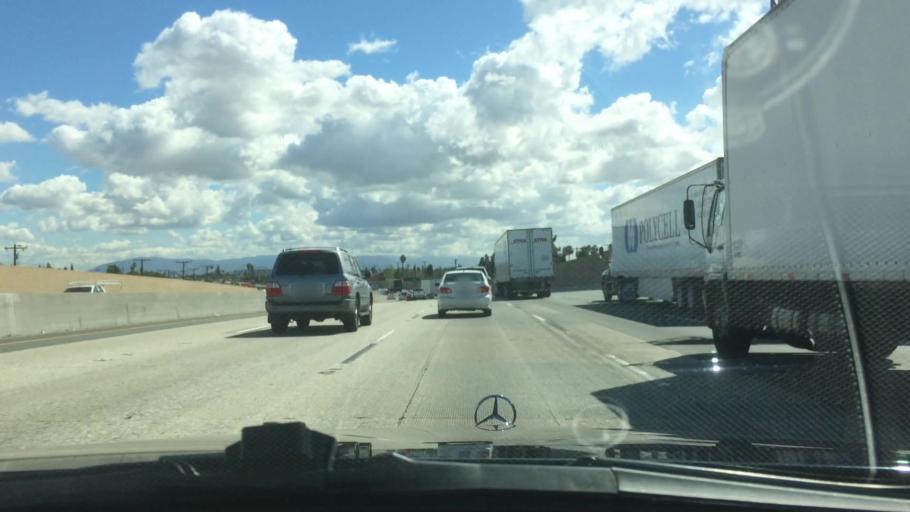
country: US
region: California
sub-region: Orange County
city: Buena Park
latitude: 33.8545
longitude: -117.9676
